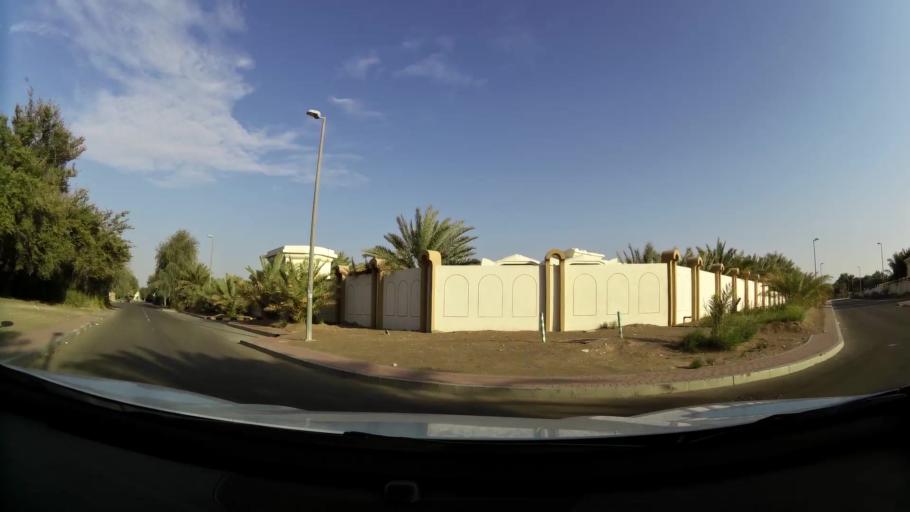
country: AE
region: Abu Dhabi
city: Al Ain
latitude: 24.0821
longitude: 55.8434
